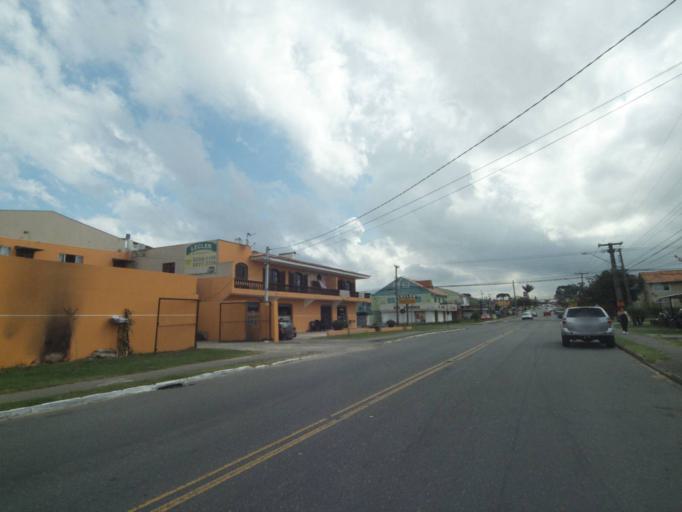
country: BR
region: Parana
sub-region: Pinhais
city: Pinhais
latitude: -25.4505
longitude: -49.2074
